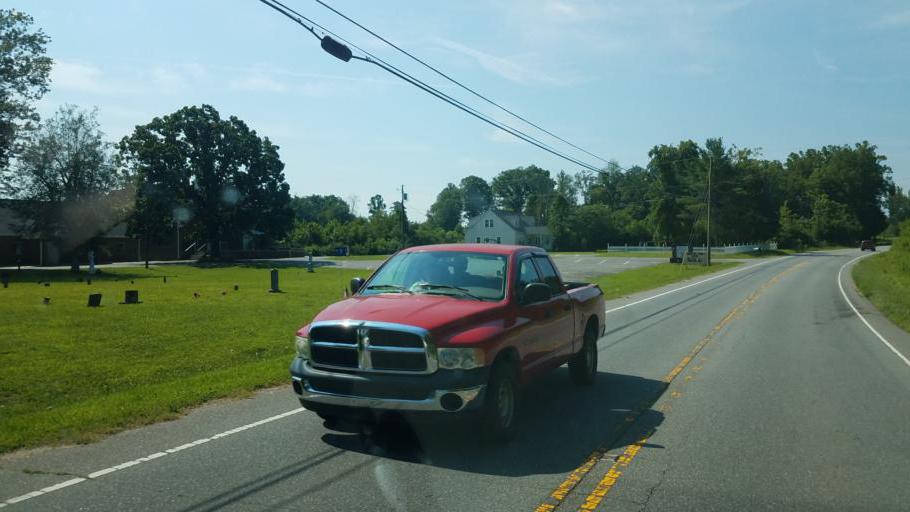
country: US
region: North Carolina
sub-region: Burke County
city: Glen Alpine
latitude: 35.7870
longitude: -81.7579
